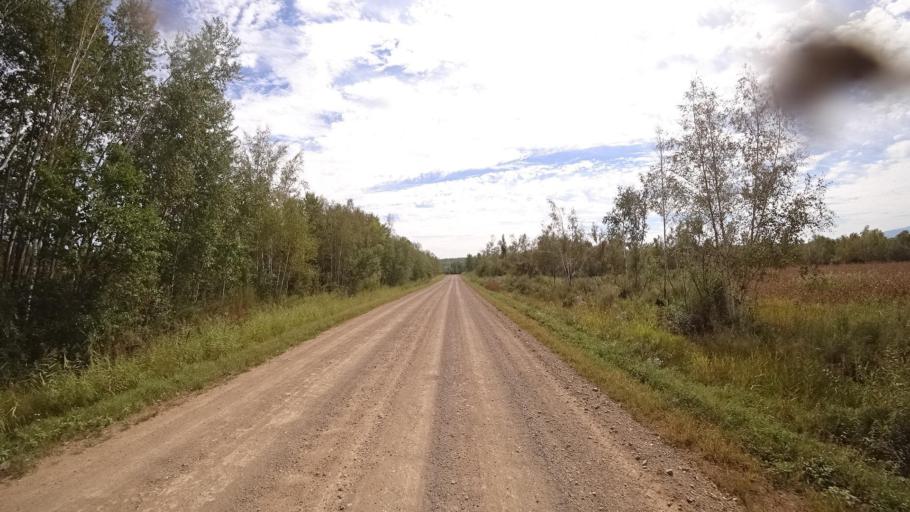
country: RU
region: Primorskiy
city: Yakovlevka
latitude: 44.5663
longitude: 133.5955
